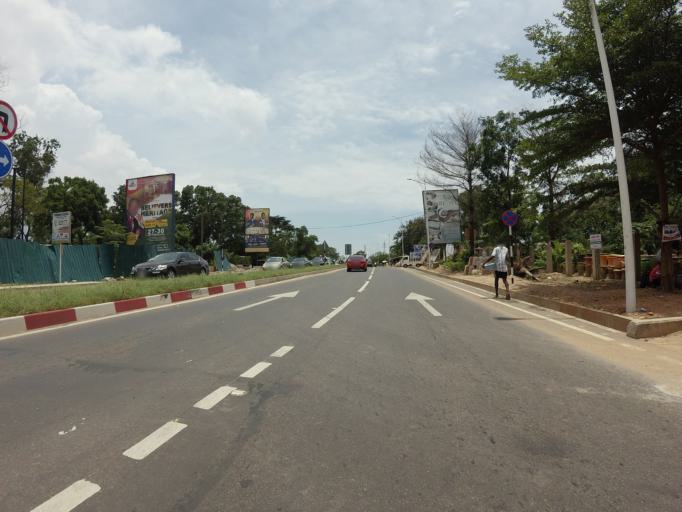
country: GH
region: Greater Accra
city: Medina Estates
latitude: 5.6305
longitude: -0.1567
